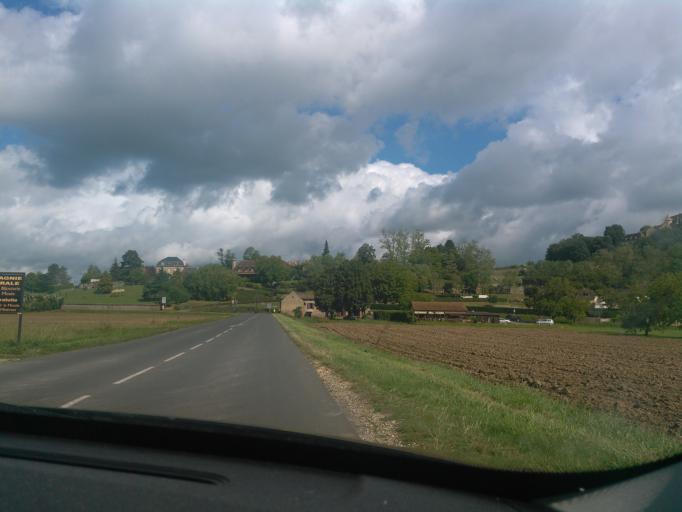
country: FR
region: Aquitaine
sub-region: Departement de la Dordogne
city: Cenac-et-Saint-Julien
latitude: 44.8211
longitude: 1.1567
